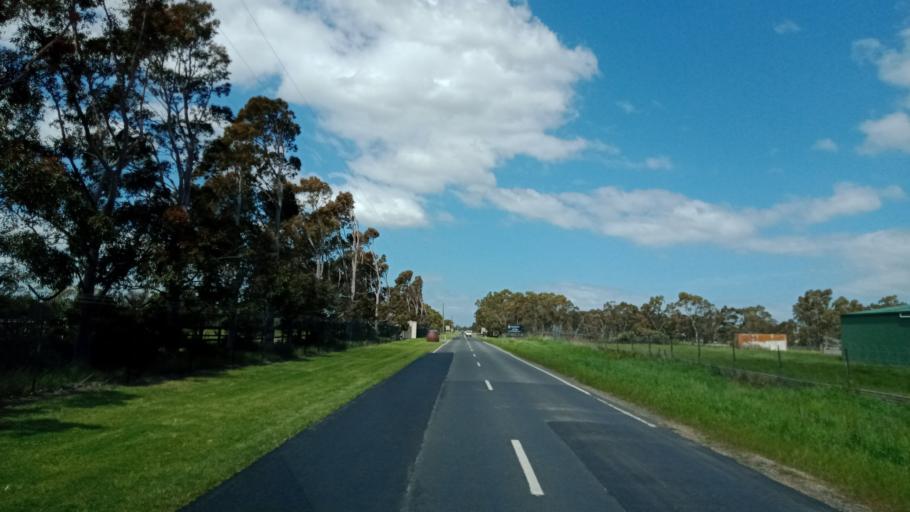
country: AU
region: Victoria
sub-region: Kingston
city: Chelsea Heights
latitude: -38.0452
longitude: 145.1485
